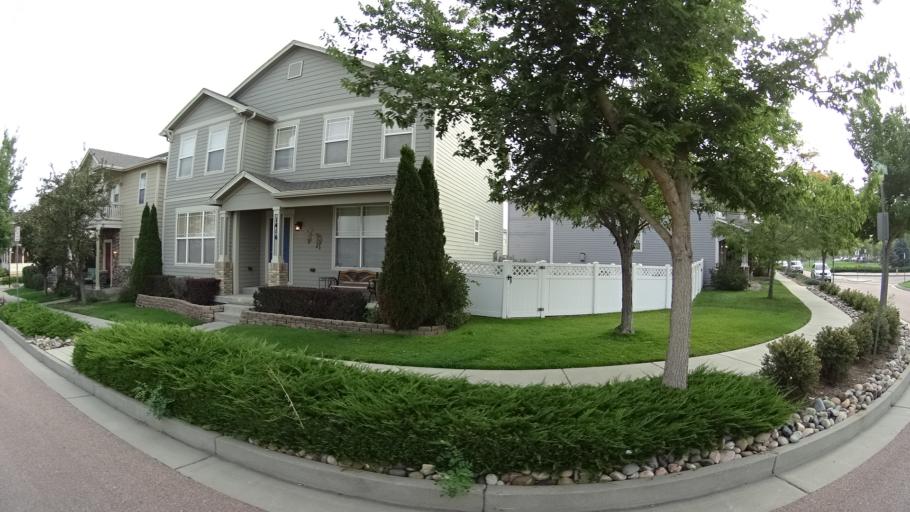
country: US
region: Colorado
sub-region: El Paso County
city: Stratmoor
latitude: 38.8099
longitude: -104.7872
